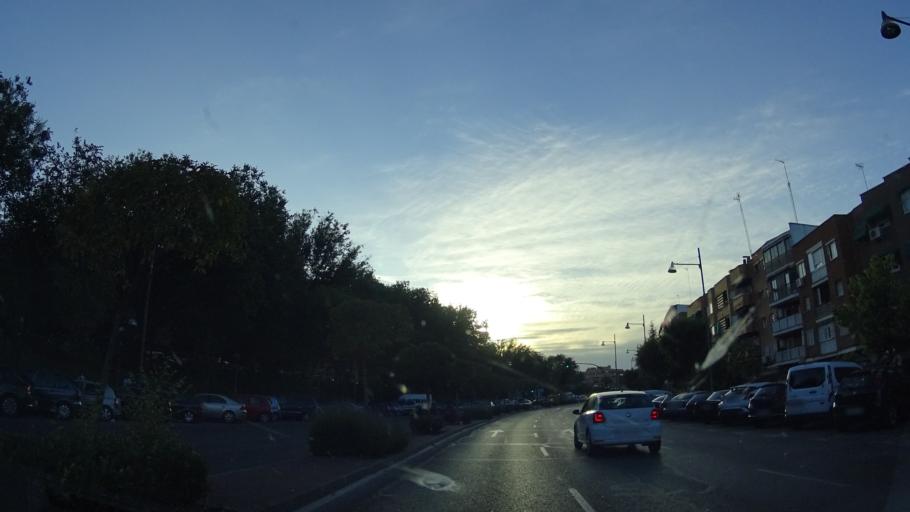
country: ES
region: Madrid
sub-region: Provincia de Madrid
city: Alcobendas
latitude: 40.5451
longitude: -3.6324
